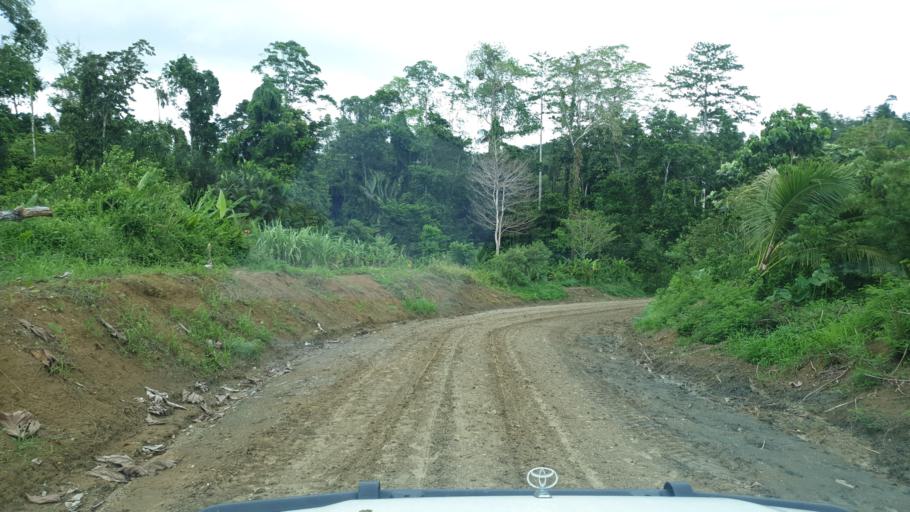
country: PG
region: Gulf
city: Kerema
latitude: -7.9823
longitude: 145.8354
